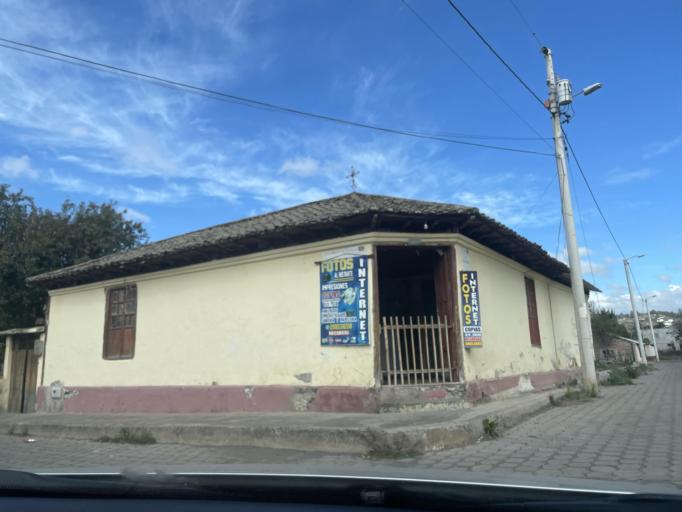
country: EC
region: Chimborazo
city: Guano
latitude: -1.6064
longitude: -78.6310
